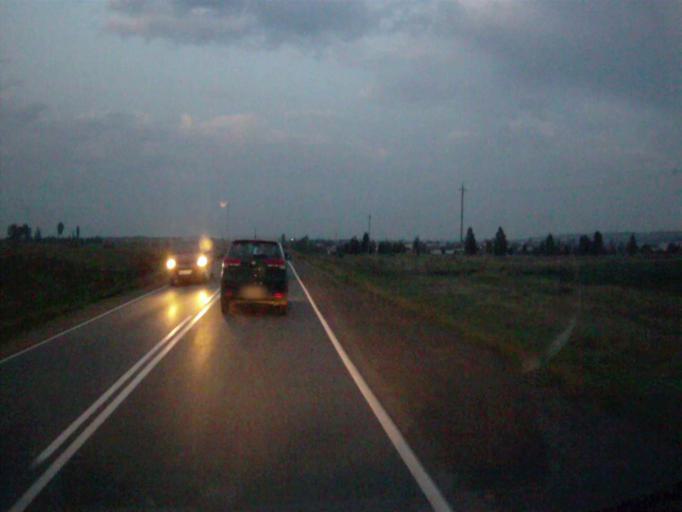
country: RU
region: Chelyabinsk
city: Poletayevo
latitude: 55.2103
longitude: 60.8989
